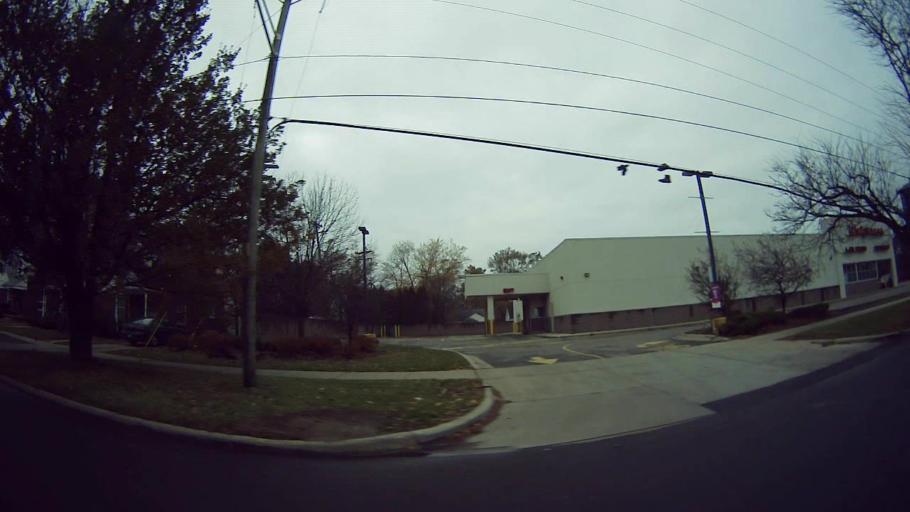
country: US
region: Michigan
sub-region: Oakland County
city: Southfield
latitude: 42.4286
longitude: -83.2388
